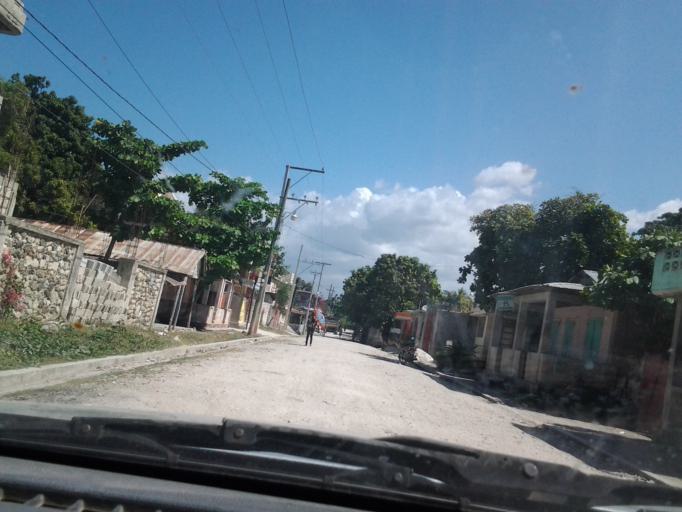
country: HT
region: Ouest
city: Grangwav
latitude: 18.4270
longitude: -72.7702
